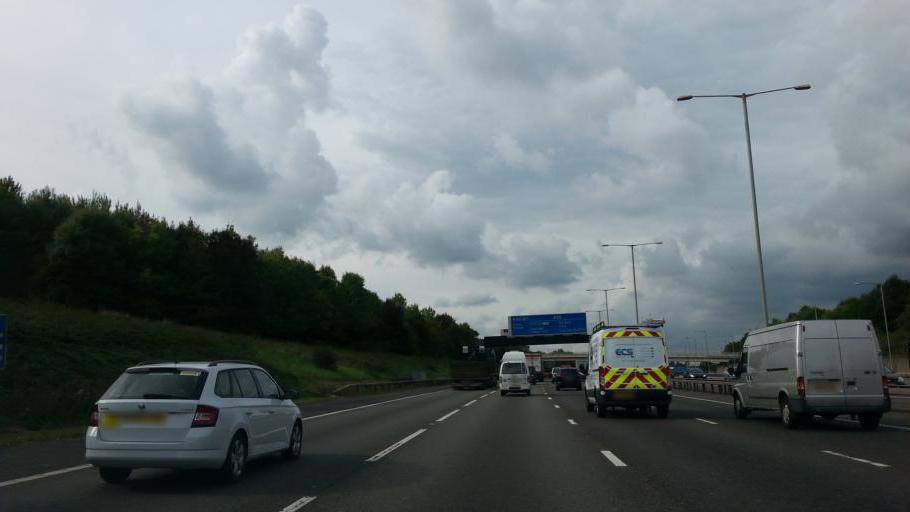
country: GB
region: England
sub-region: Buckinghamshire
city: Denham
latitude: 51.5502
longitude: -0.5228
